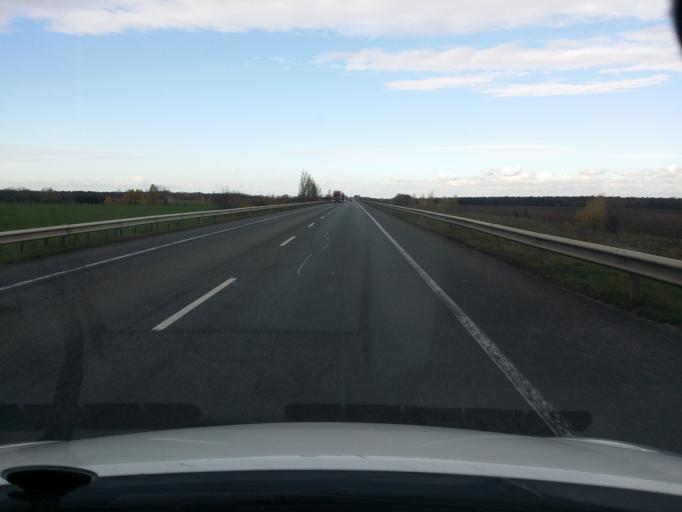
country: HU
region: Gyor-Moson-Sopron
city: Rajka
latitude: 47.9244
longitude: 17.1744
